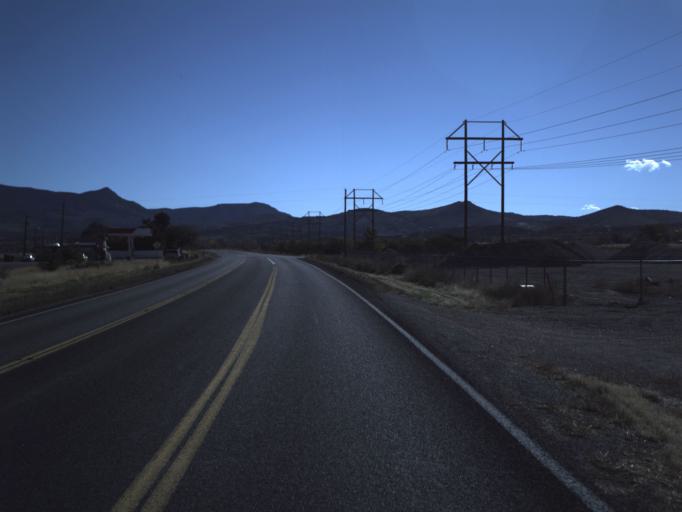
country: US
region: Utah
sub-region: Washington County
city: Enterprise
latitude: 37.6722
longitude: -113.5507
